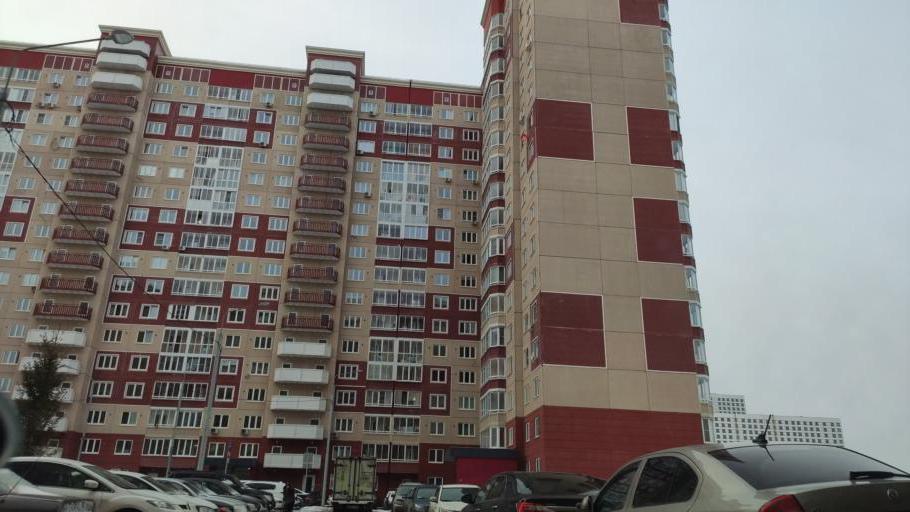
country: RU
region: Moscow
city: Annino
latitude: 55.5344
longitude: 37.6207
